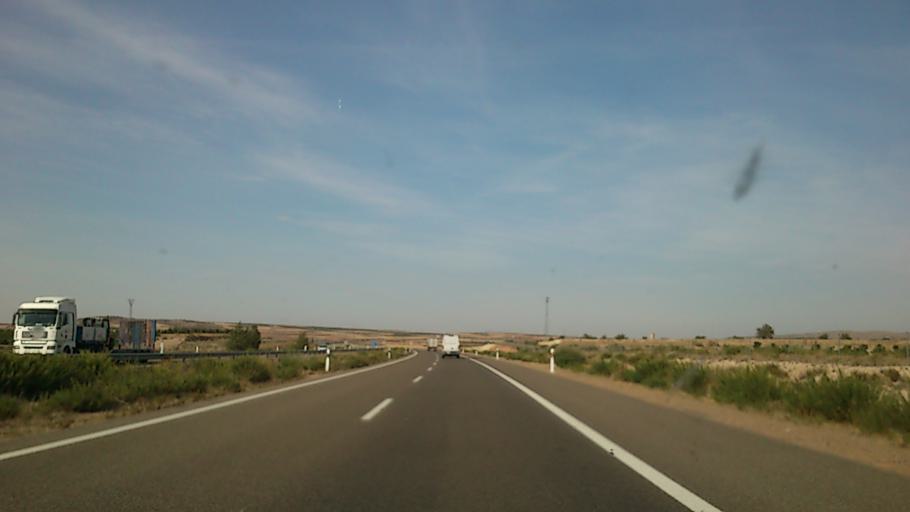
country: ES
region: Aragon
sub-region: Provincia de Zaragoza
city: Longares
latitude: 41.3887
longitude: -1.1841
